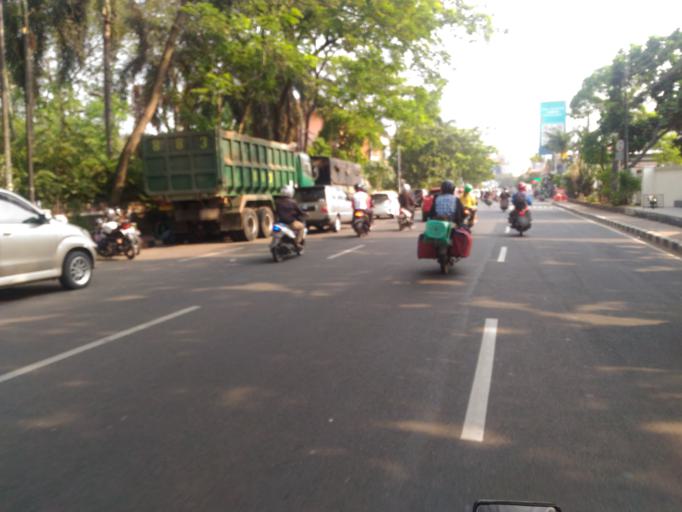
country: ID
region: Banten
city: Tangerang
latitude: -6.1702
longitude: 106.6327
